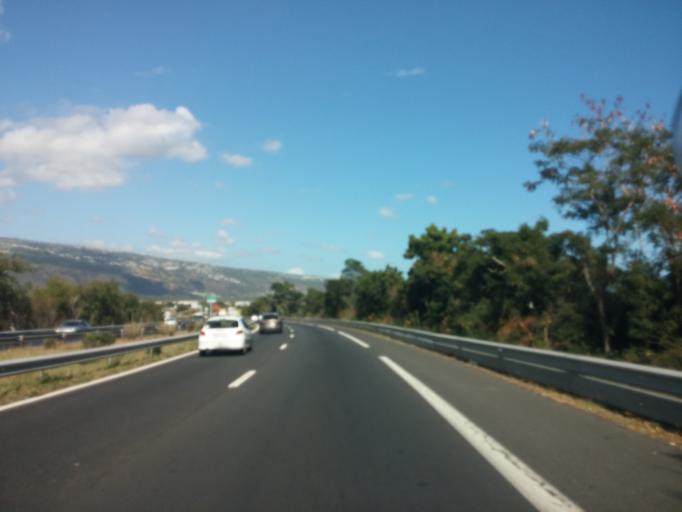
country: RE
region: Reunion
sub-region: Reunion
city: Le Port
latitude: -20.9657
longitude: 55.2992
